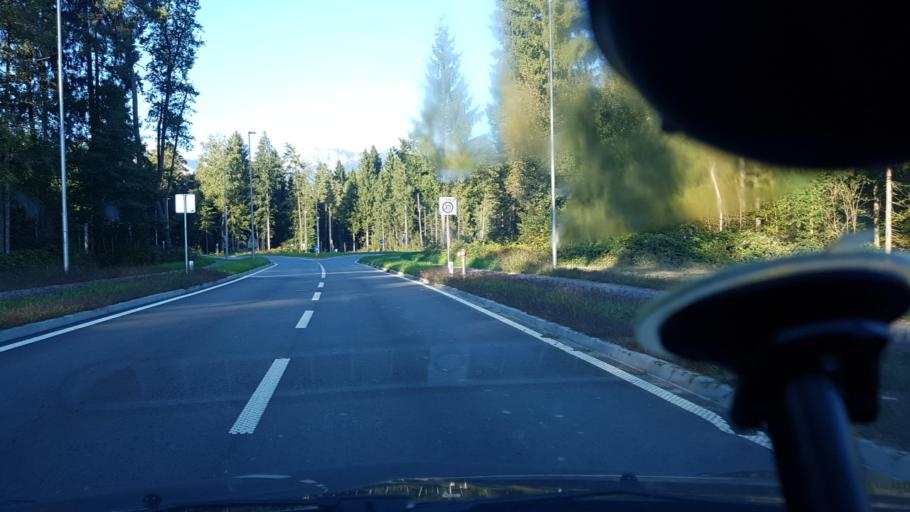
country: SI
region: Cerklje na Gorenjskem
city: Cerklje na Gorenjskem
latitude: 46.2335
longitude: 14.4594
